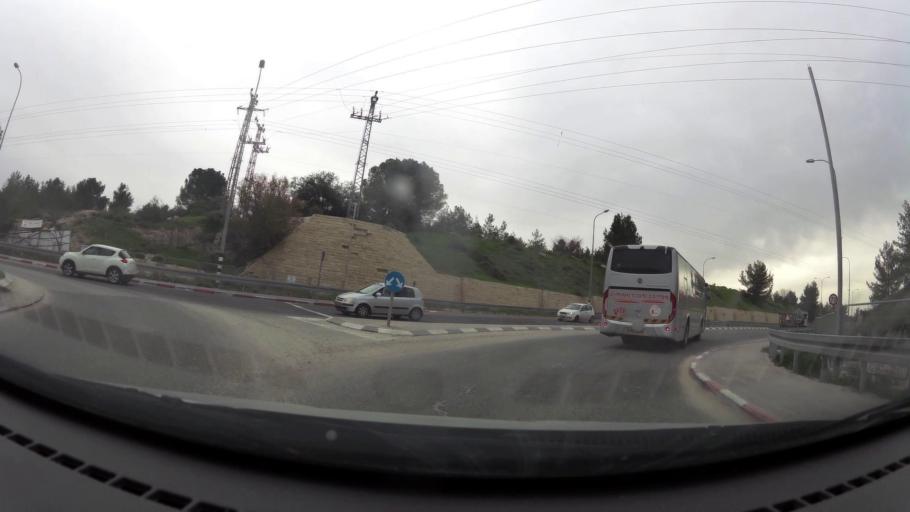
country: IL
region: Jerusalem
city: Bet Shemesh
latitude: 31.7006
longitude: 35.0088
